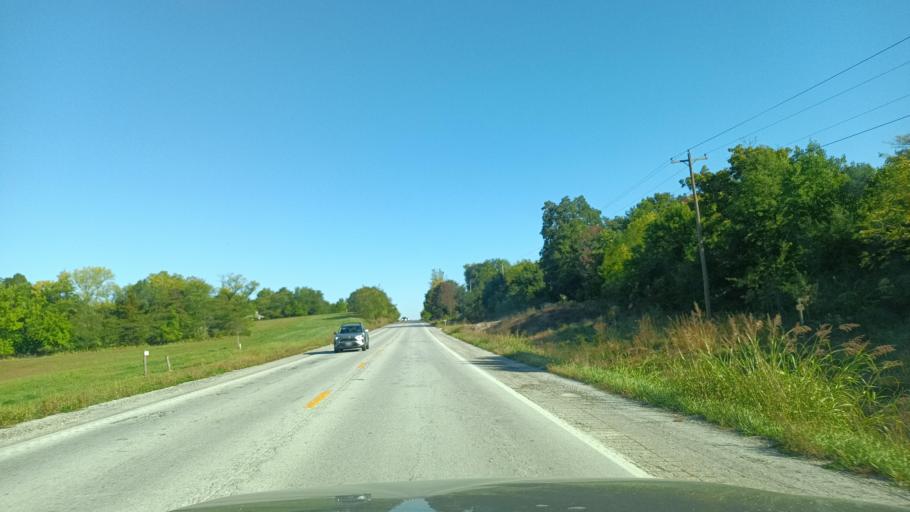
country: US
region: Missouri
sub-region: Audrain County
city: Vandalia
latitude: 39.3912
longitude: -91.6418
